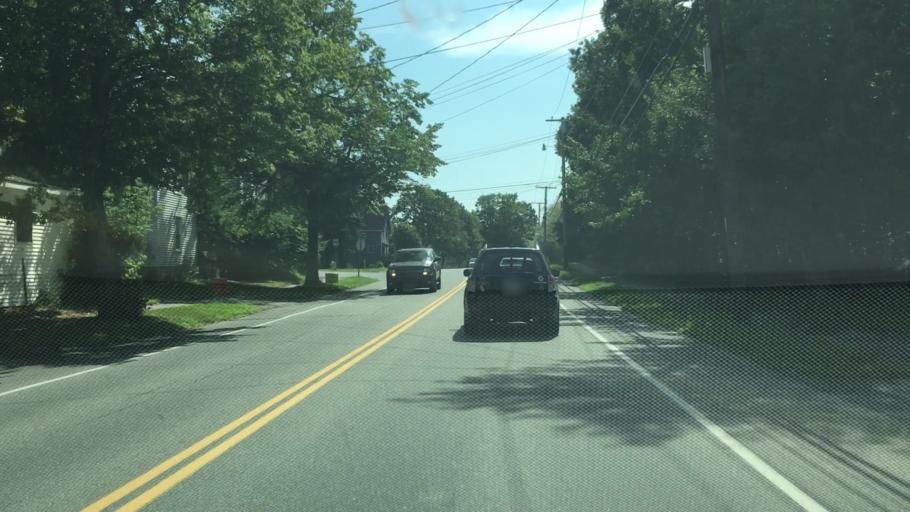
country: US
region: Maine
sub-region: Penobscot County
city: Brewer
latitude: 44.8169
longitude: -68.7646
